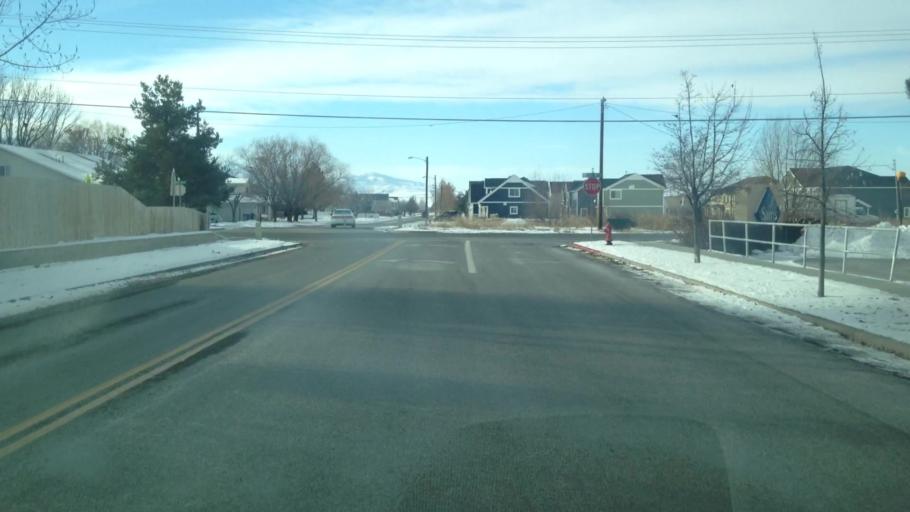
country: US
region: Utah
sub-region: Cache County
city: Logan
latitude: 41.7540
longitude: -111.8387
